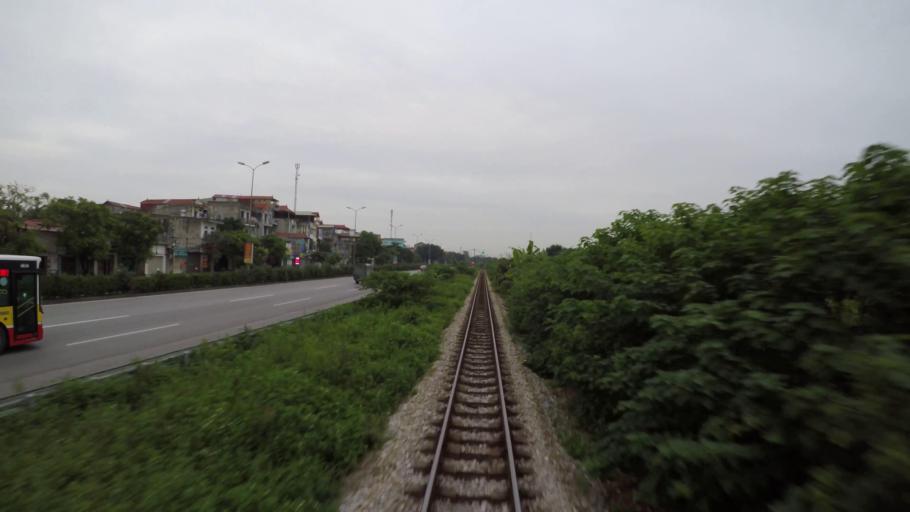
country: VN
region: Ha Noi
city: Trau Quy
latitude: 21.0120
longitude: 105.9507
